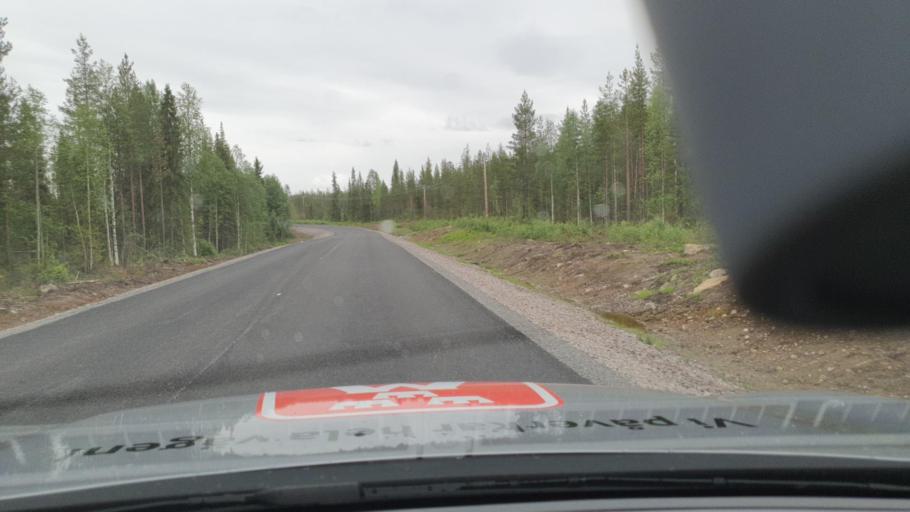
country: SE
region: Norrbotten
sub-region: Overkalix Kommun
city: OEverkalix
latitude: 66.6606
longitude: 23.2204
